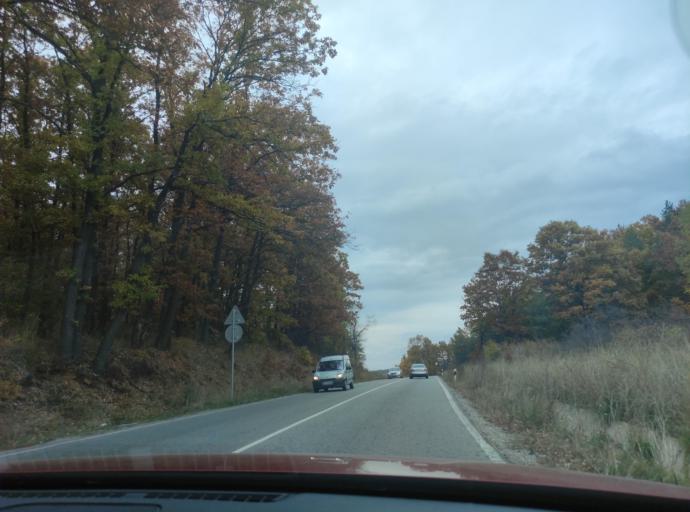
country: BG
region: Sofiya
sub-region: Obshtina Godech
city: Godech
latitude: 42.9446
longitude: 23.1598
